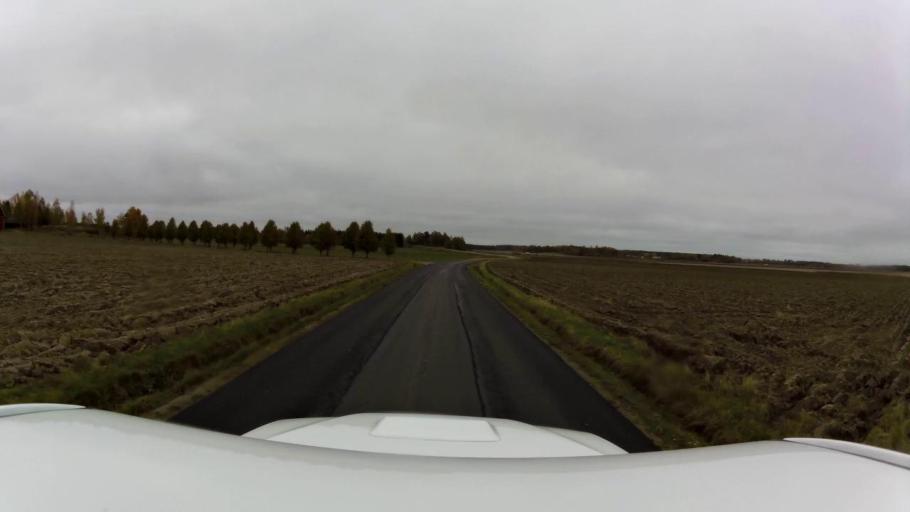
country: SE
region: OEstergoetland
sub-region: Linkopings Kommun
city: Linghem
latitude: 58.4473
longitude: 15.7113
